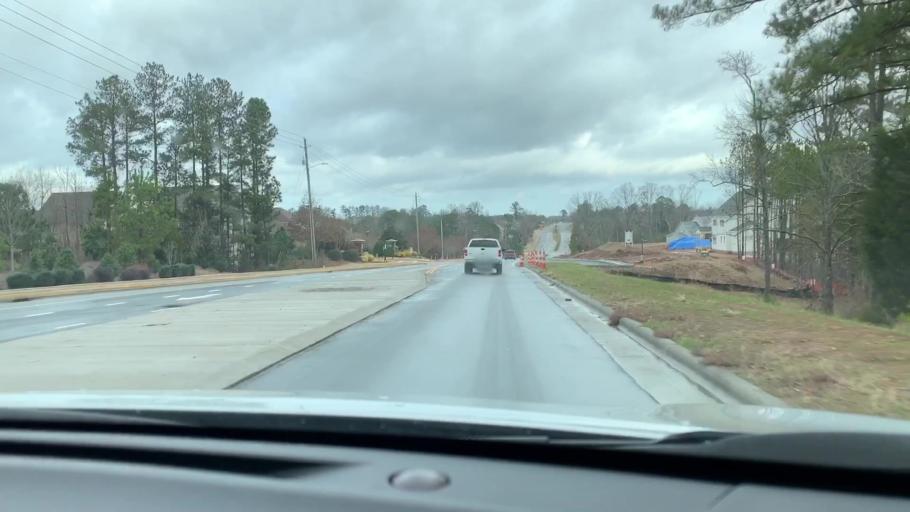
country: US
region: North Carolina
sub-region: Wake County
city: Green Level
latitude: 35.8338
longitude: -78.8993
